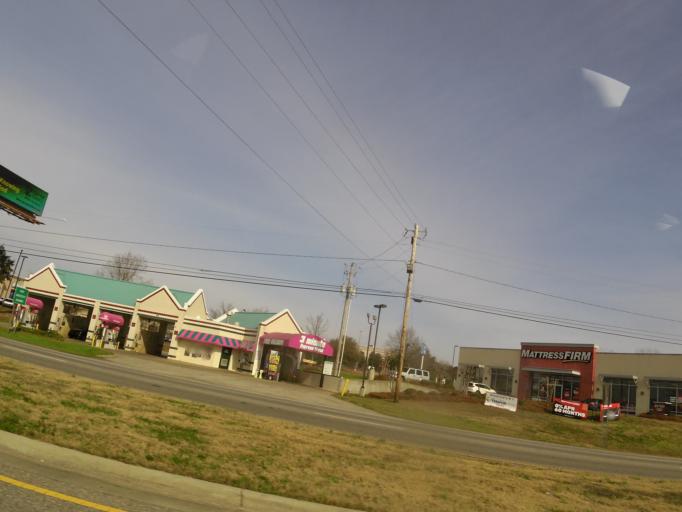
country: US
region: Alabama
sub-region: Houston County
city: Dothan
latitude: 31.2503
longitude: -85.4261
